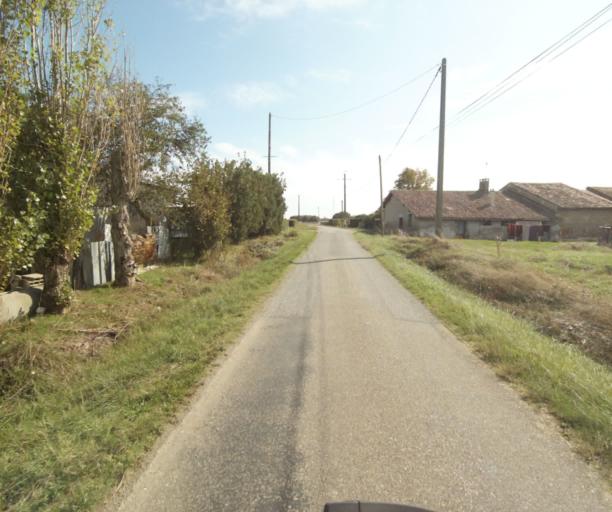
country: FR
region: Midi-Pyrenees
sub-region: Departement du Tarn-et-Garonne
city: Verdun-sur-Garonne
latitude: 43.8441
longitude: 1.1758
